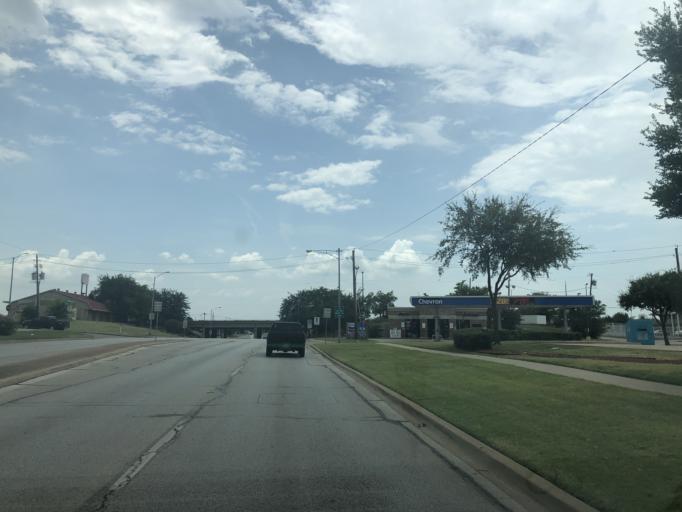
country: US
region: Texas
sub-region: Dallas County
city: Grand Prairie
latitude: 32.7438
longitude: -97.0164
